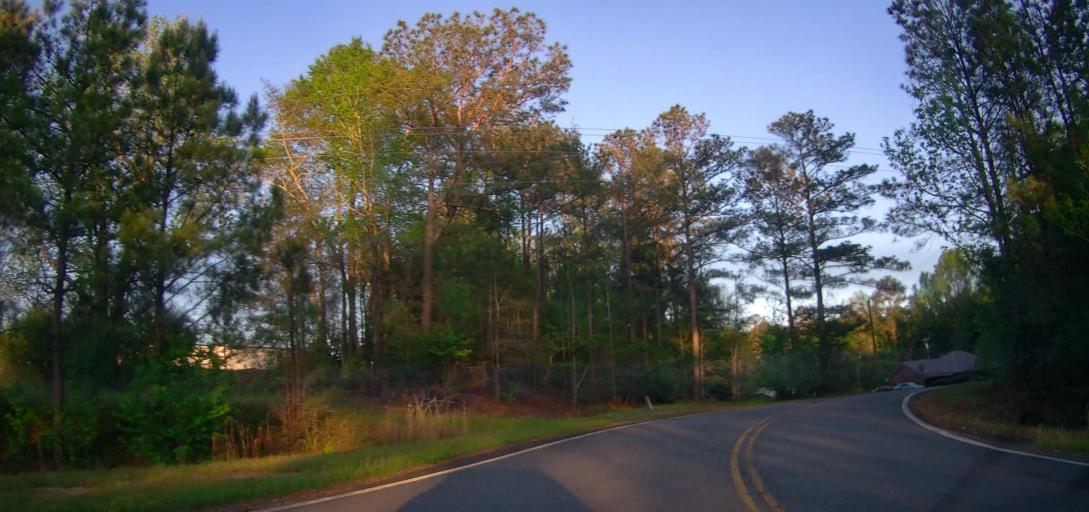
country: US
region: Georgia
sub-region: Talbot County
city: Talbotton
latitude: 32.5358
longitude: -84.6032
